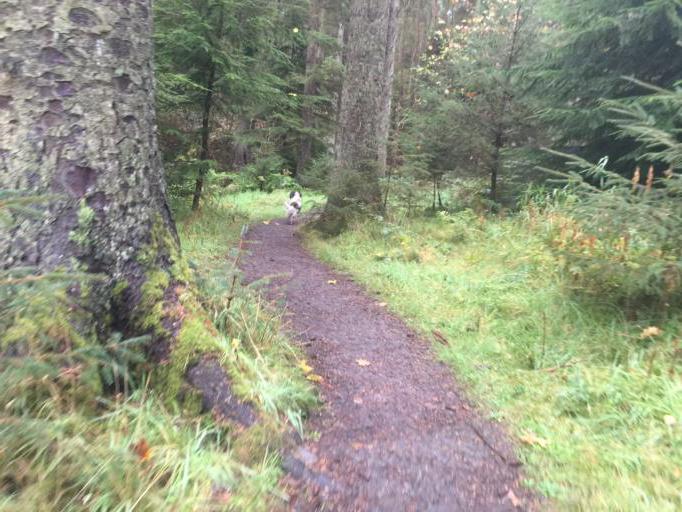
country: GB
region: Scotland
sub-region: West Lothian
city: Linlithgow
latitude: 55.9504
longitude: -3.5886
